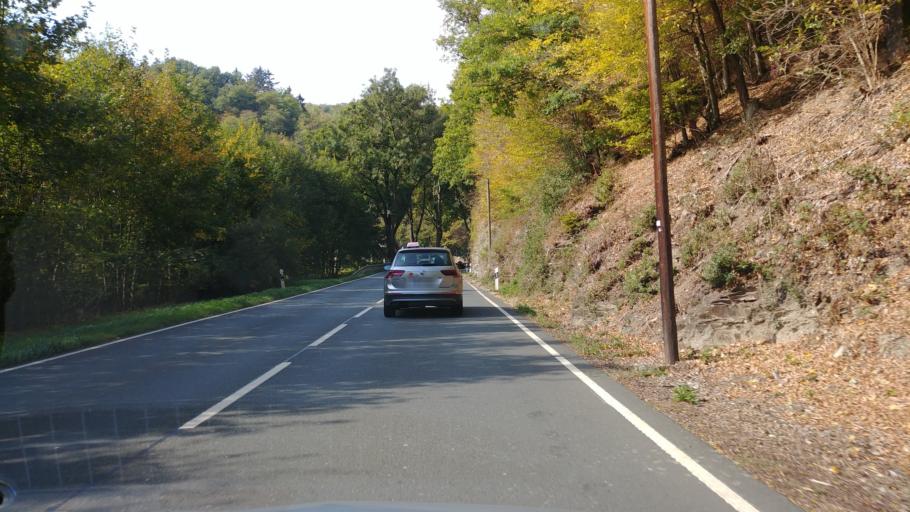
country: DE
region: Hesse
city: Burg Hohenstein
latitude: 50.1744
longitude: 8.0721
